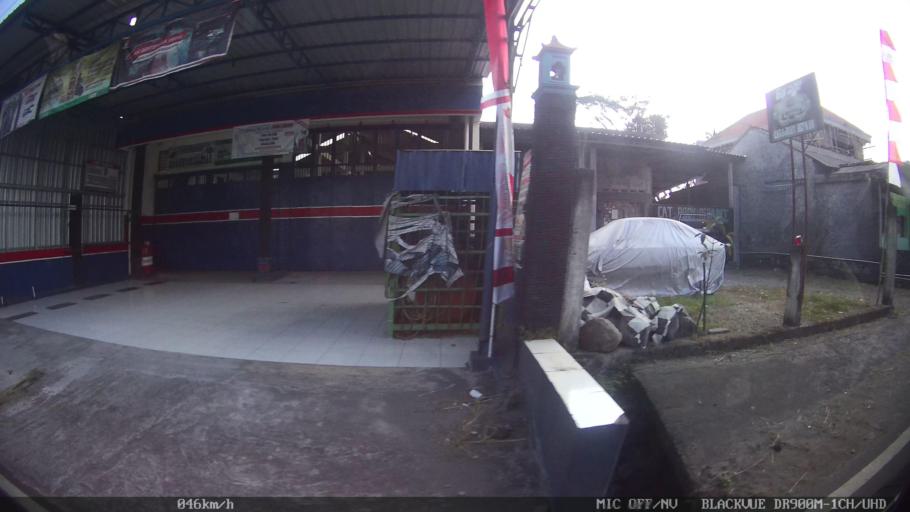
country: ID
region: Central Java
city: Candi Prambanan
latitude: -7.7060
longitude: 110.4680
